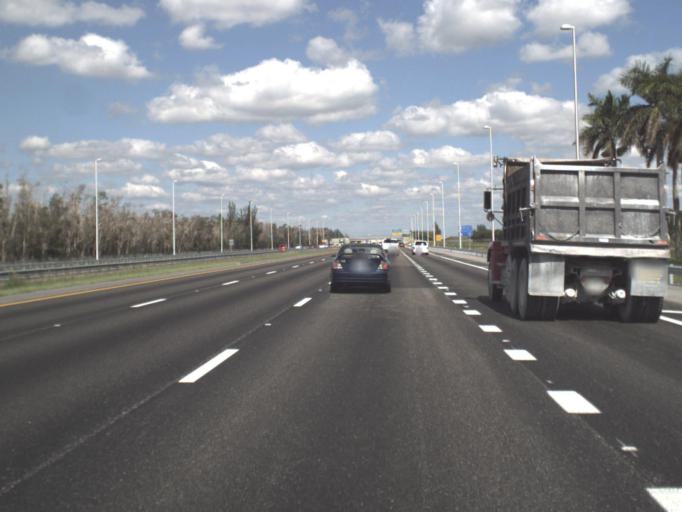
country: US
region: Florida
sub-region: Miami-Dade County
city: Doral
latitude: 25.8599
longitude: -80.3875
